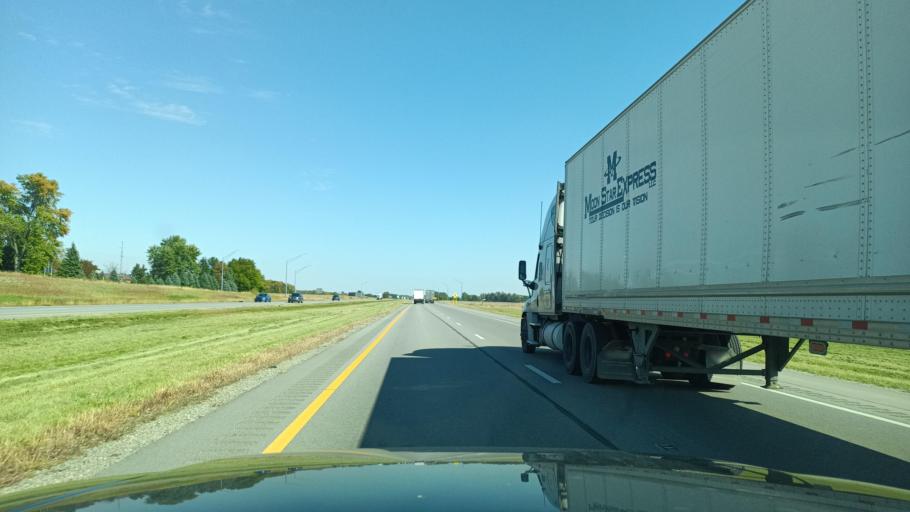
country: US
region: Ohio
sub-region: Defiance County
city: Defiance
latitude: 41.3119
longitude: -84.3230
